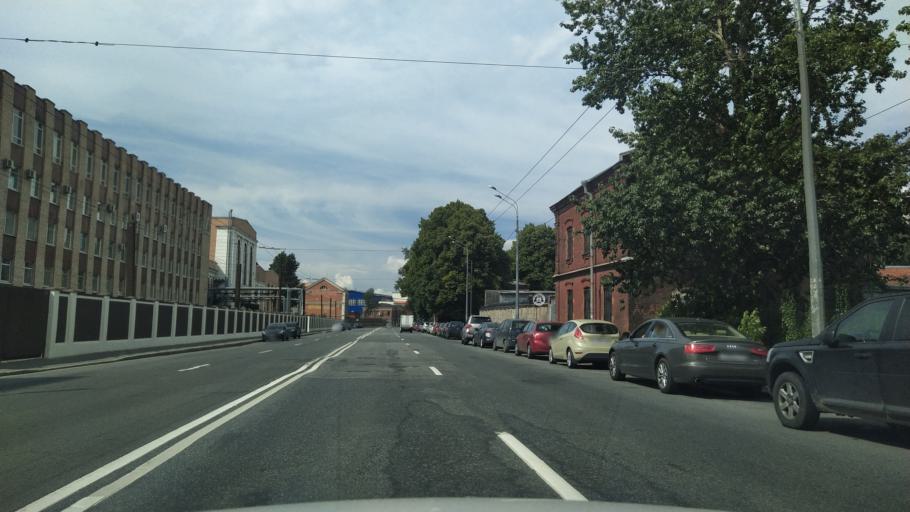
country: RU
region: Leningrad
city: Finlyandskiy
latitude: 59.9585
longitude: 30.3711
